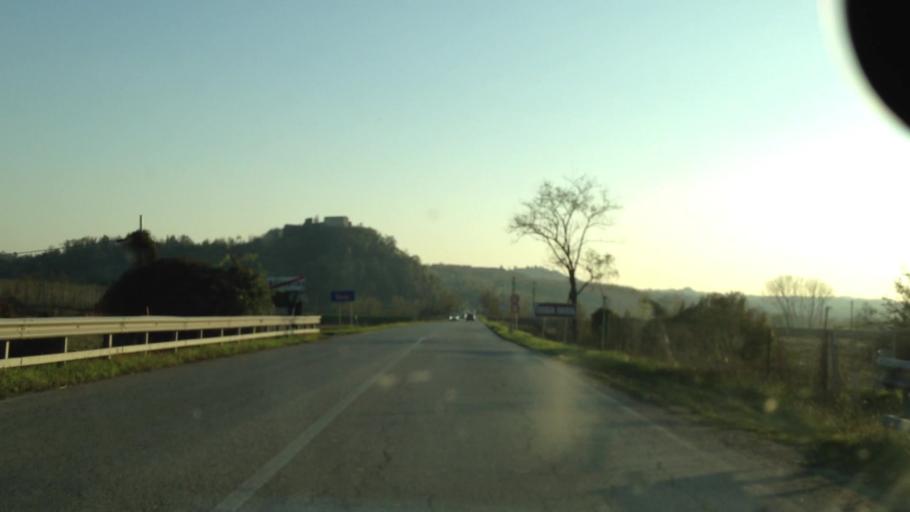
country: IT
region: Piedmont
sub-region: Provincia di Vercelli
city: Crescentino
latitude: 45.1845
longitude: 8.1009
